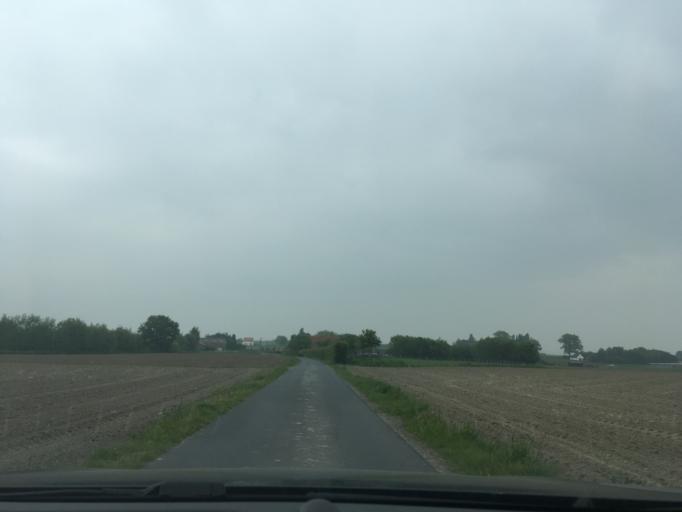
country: BE
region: Flanders
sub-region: Provincie West-Vlaanderen
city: Lichtervelde
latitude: 51.0114
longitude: 3.1311
